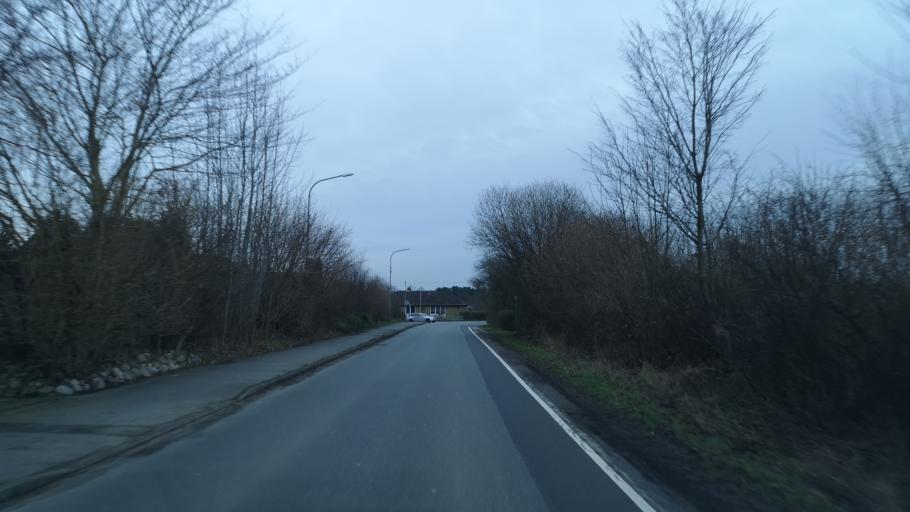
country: DE
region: Schleswig-Holstein
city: Satrup
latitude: 54.6961
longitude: 9.6098
